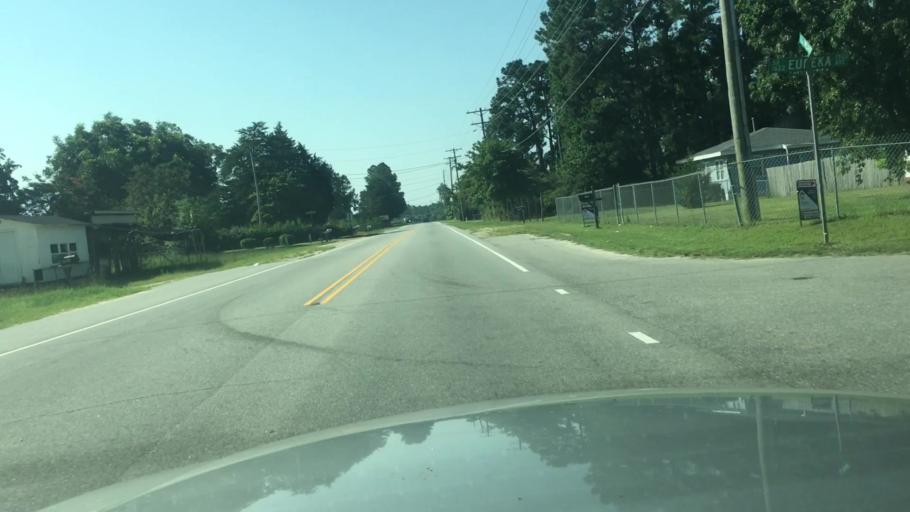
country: US
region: North Carolina
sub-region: Cumberland County
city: Spring Lake
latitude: 35.1486
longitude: -78.9115
